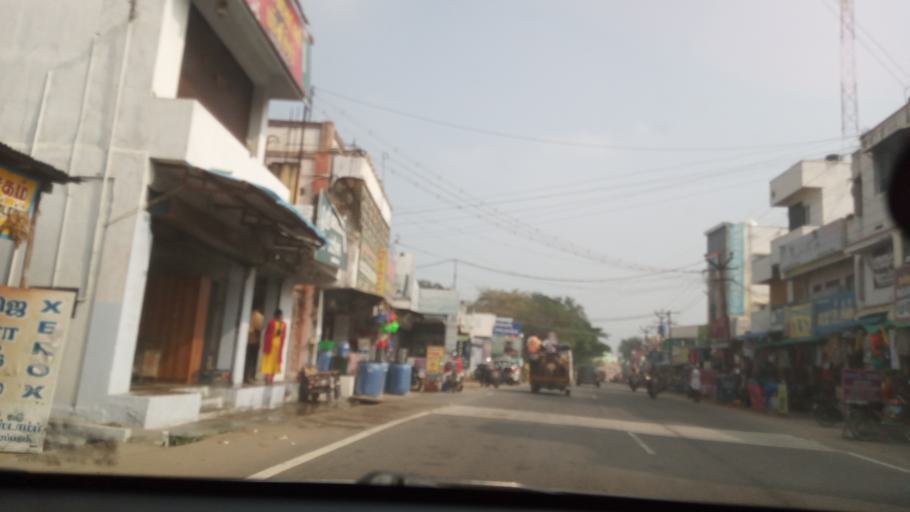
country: IN
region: Tamil Nadu
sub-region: Erode
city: Punjai Puliyampatti
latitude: 11.3515
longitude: 77.1674
